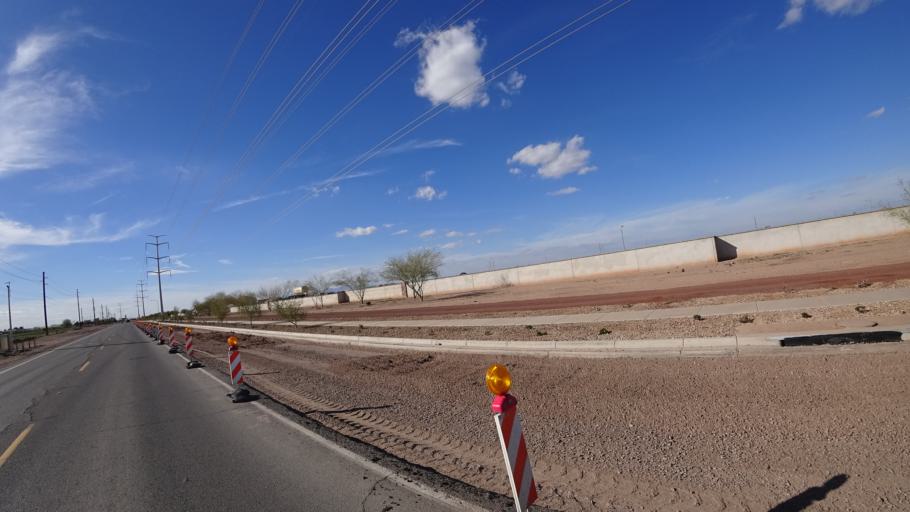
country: US
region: Arizona
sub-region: Maricopa County
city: Tolleson
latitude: 33.4085
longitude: -112.2319
